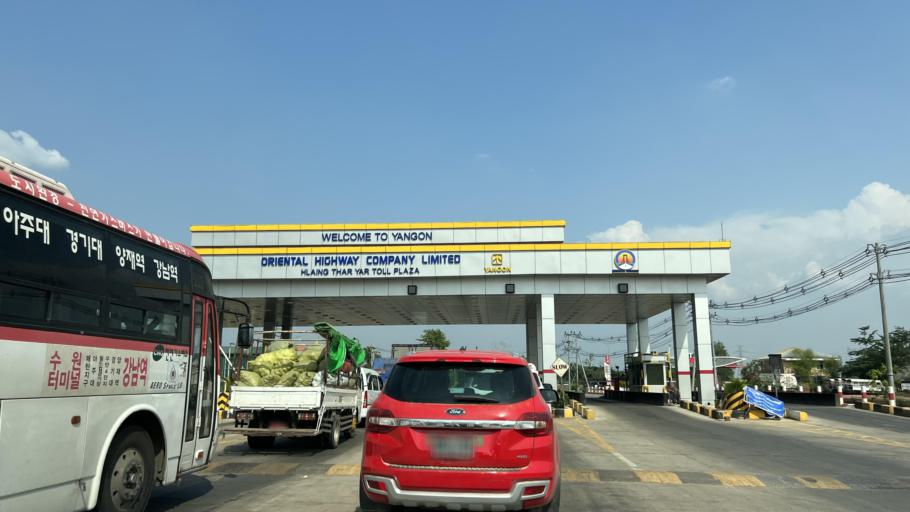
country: MM
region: Yangon
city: Yangon
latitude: 16.8894
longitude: 95.9957
